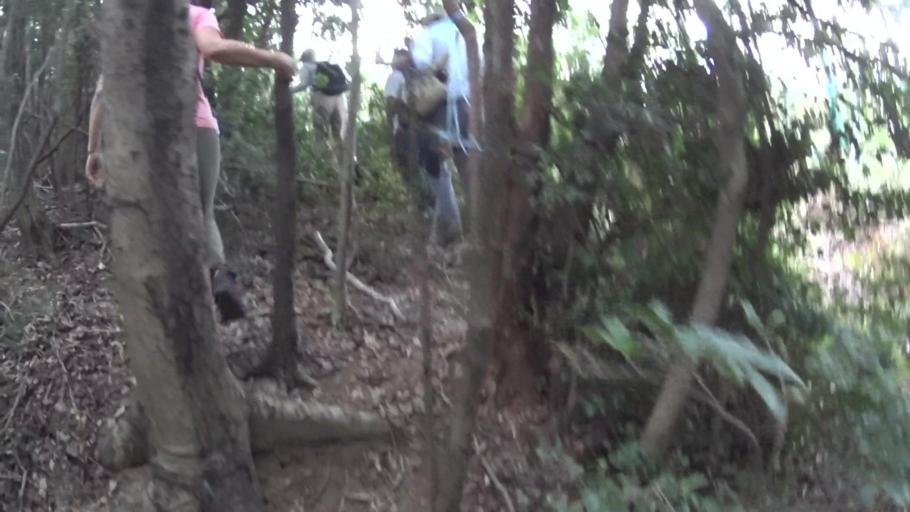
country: JP
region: Osaka
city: Kaizuka
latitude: 34.4710
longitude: 135.3036
